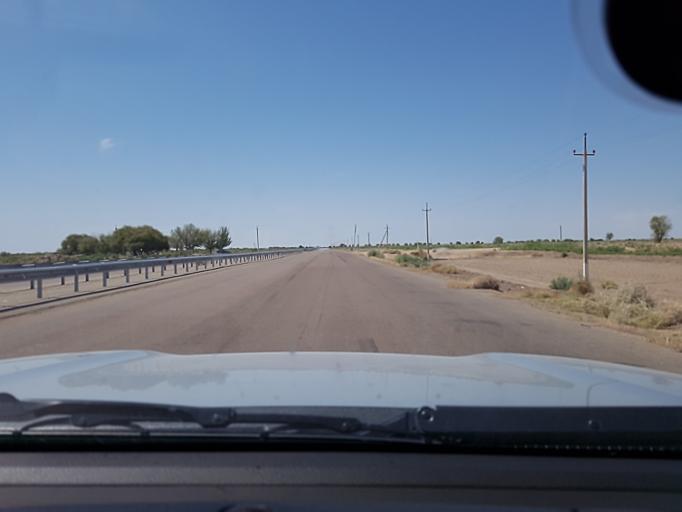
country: TM
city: Akdepe
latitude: 41.7366
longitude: 59.1055
